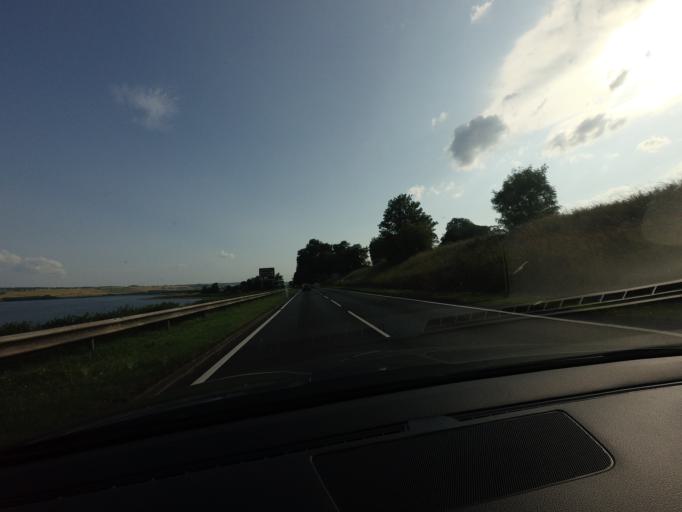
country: GB
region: Scotland
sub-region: Highland
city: Evanton
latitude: 57.6304
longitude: -4.3662
